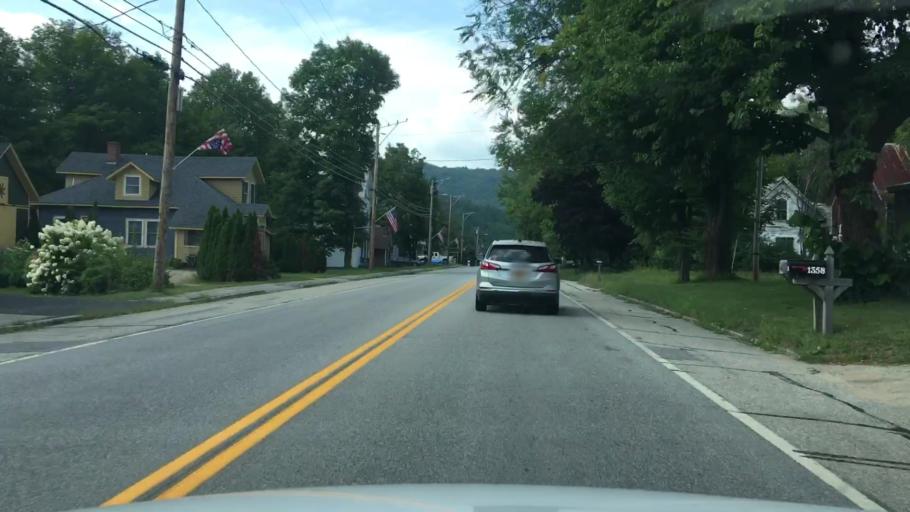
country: US
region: Maine
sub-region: Oxford County
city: Rumford
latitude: 44.5128
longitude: -70.6140
